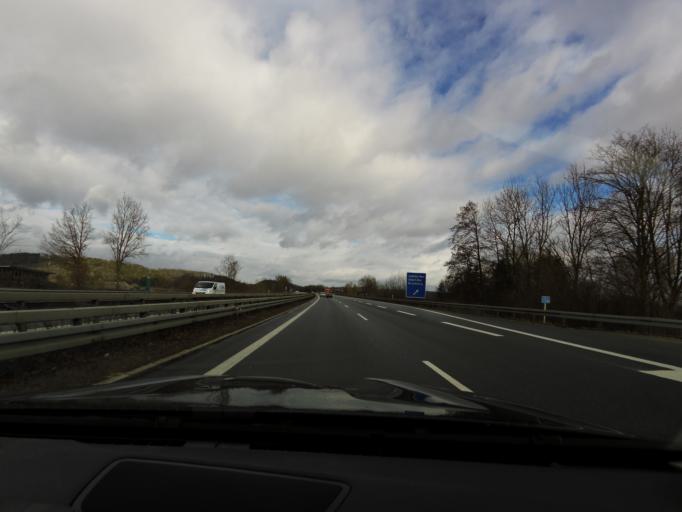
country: DE
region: Bavaria
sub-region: Lower Bavaria
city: Eching
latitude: 48.5291
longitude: 12.0707
